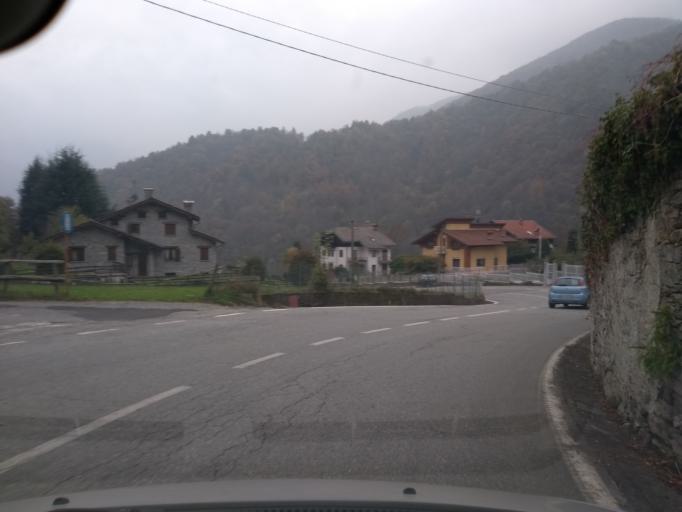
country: IT
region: Piedmont
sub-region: Provincia di Torino
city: Ceres
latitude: 45.3062
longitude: 7.3978
